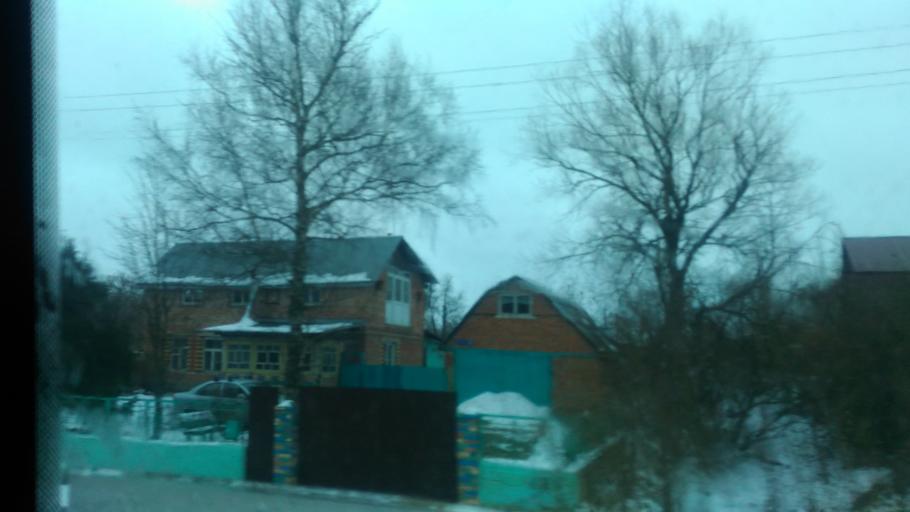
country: RU
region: Tula
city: Bolokhovo
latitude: 54.0516
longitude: 37.8183
